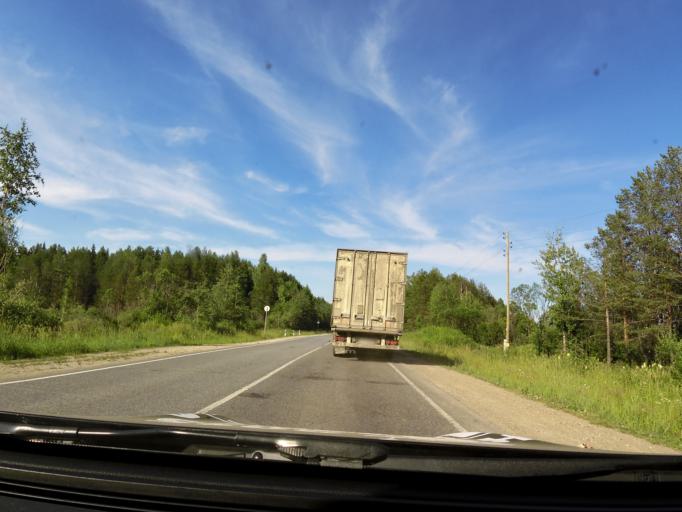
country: RU
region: Kirov
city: Belaya Kholunitsa
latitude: 58.8747
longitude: 50.8612
